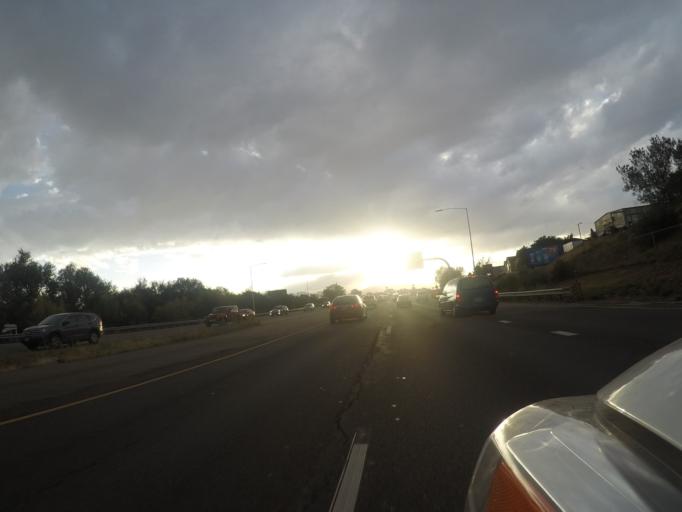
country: US
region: Colorado
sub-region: Arapahoe County
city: Sheridan
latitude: 39.6525
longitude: -105.0213
